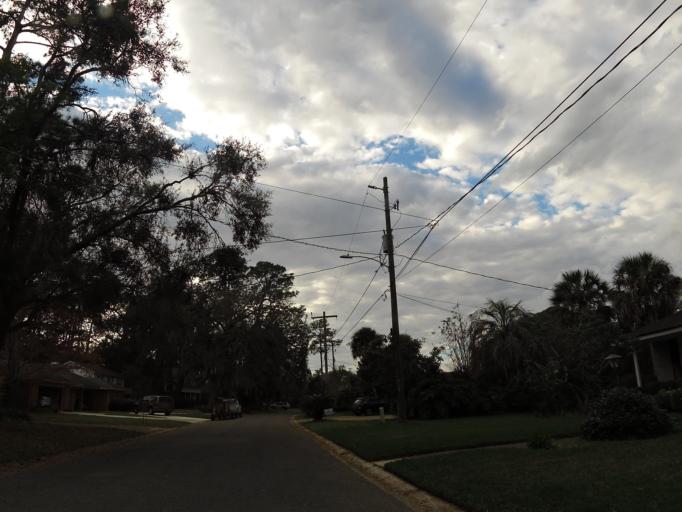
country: US
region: Florida
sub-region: Duval County
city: Jacksonville
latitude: 30.2495
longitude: -81.6354
